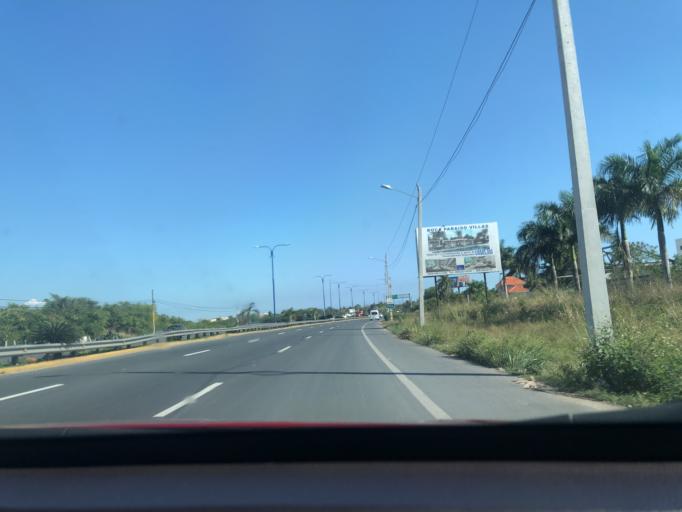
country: DO
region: Santo Domingo
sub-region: Santo Domingo
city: Boca Chica
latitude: 18.4539
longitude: -69.6010
